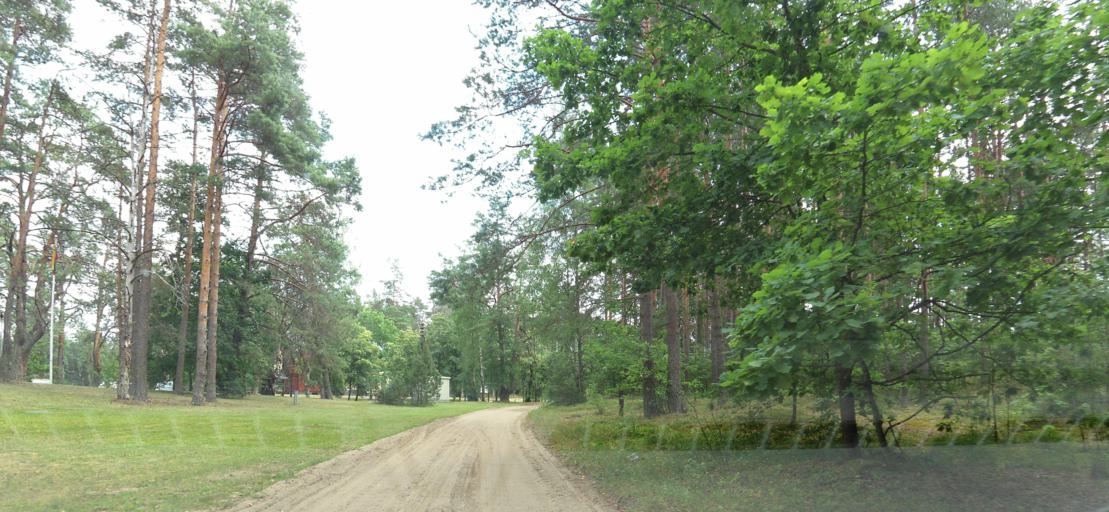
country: LT
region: Alytaus apskritis
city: Varena
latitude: 54.0610
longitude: 24.3981
